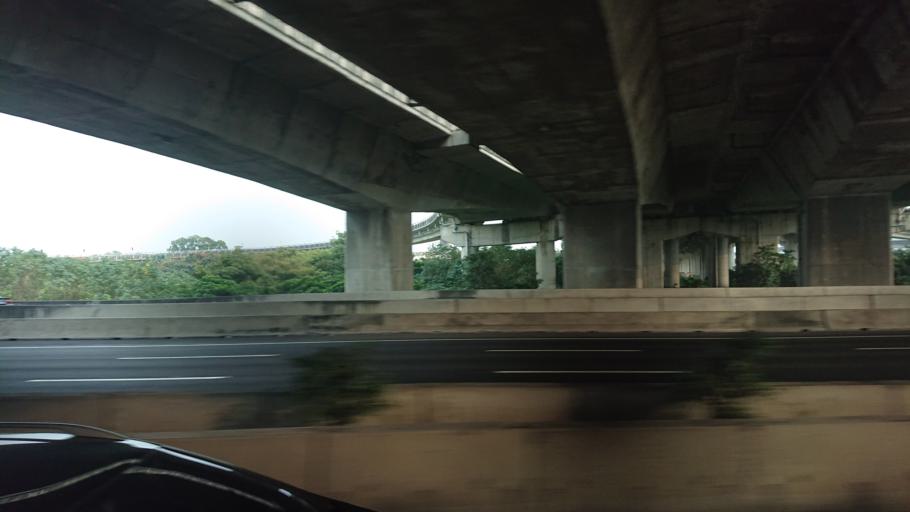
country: TW
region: Taiwan
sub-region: Yunlin
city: Douliu
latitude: 23.6681
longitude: 120.4563
